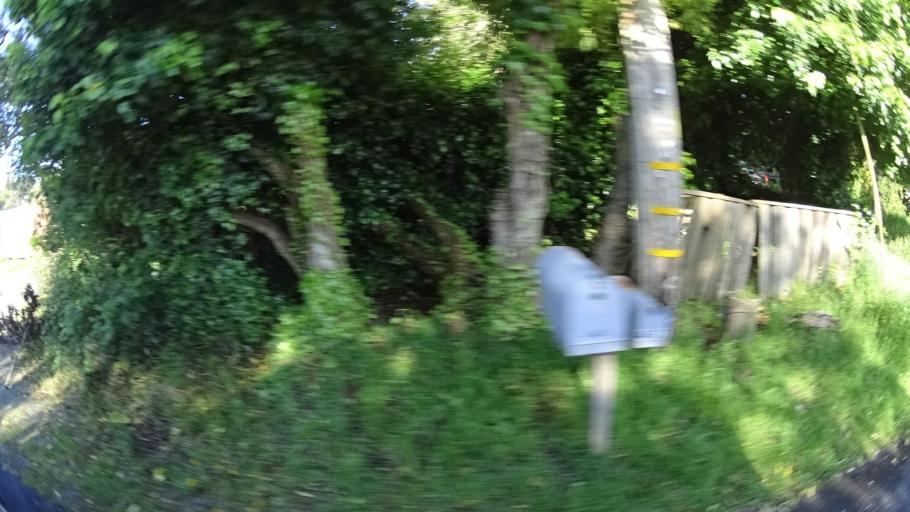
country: US
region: California
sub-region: Humboldt County
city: McKinleyville
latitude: 40.9898
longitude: -124.1005
